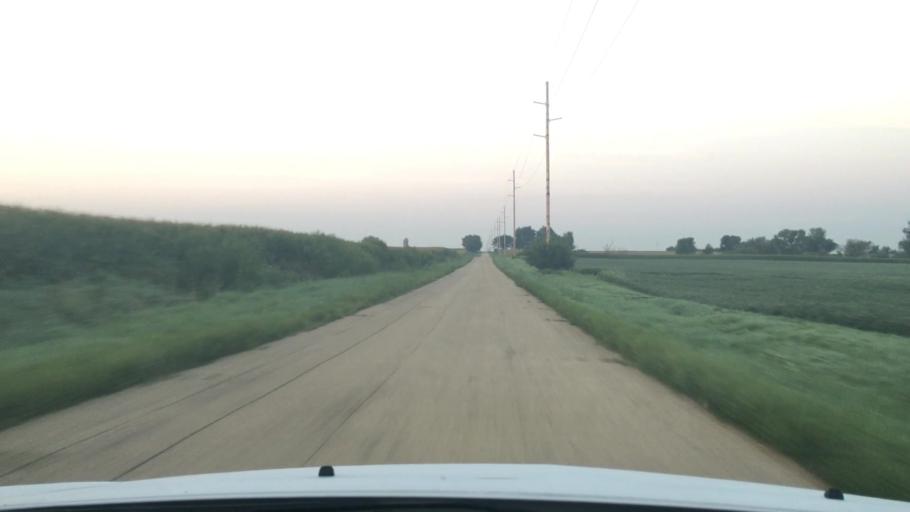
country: US
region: Illinois
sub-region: Ogle County
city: Rochelle
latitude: 41.8686
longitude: -89.0008
